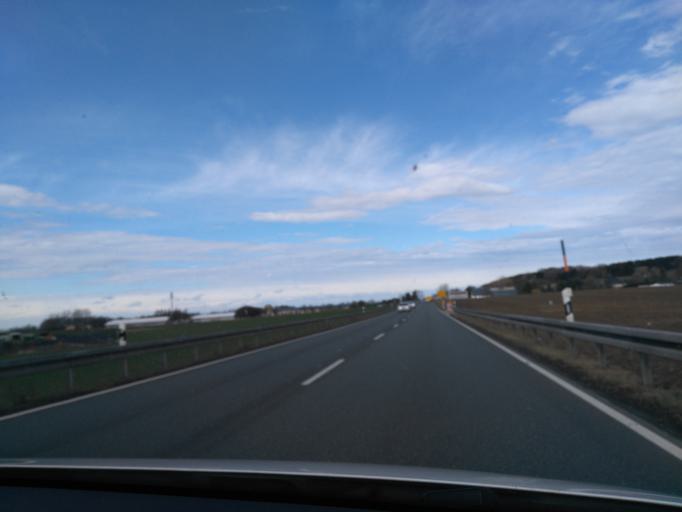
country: DE
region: Saxony
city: Grossruckerswalde
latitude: 50.6765
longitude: 13.1231
